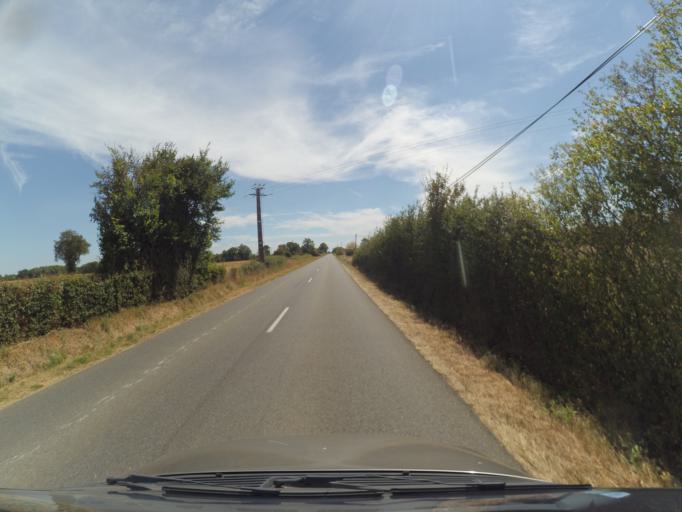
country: FR
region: Poitou-Charentes
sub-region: Departement de la Vienne
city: Availles-Limouzine
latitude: 46.1611
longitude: 0.5499
